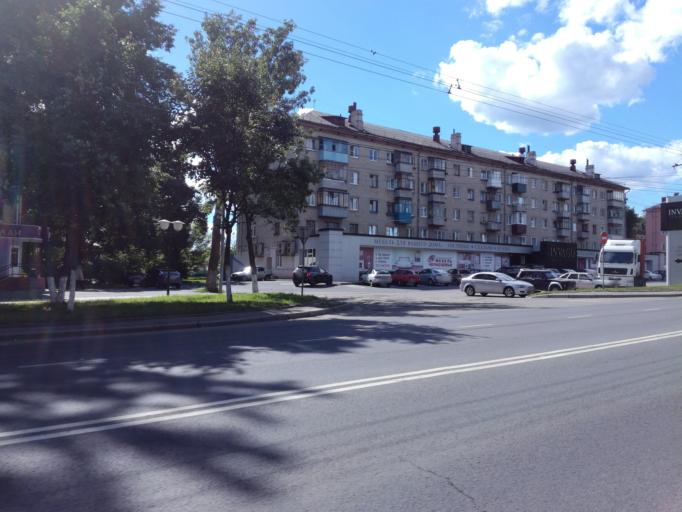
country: RU
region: Kursk
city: Kursk
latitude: 51.7689
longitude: 36.1819
